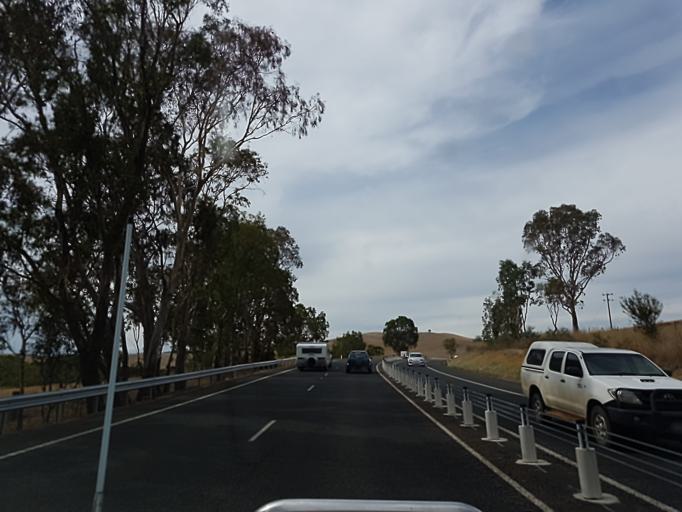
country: AU
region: Victoria
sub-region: Murrindindi
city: Alexandra
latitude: -37.1974
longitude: 145.4737
